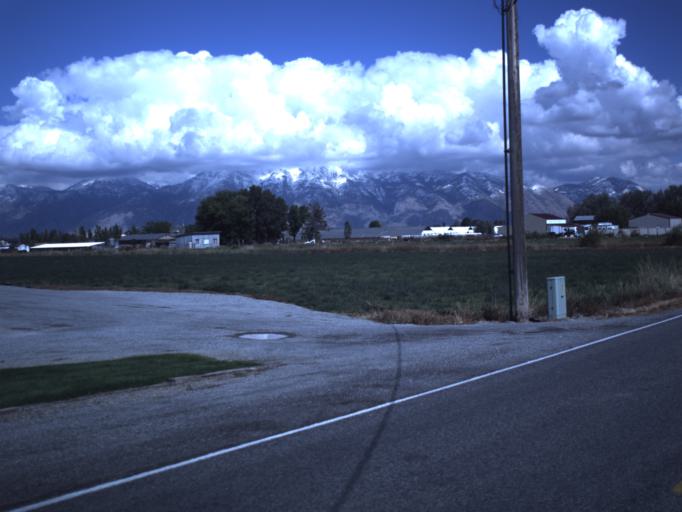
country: US
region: Utah
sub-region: Utah County
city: Benjamin
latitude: 40.1147
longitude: -111.7237
